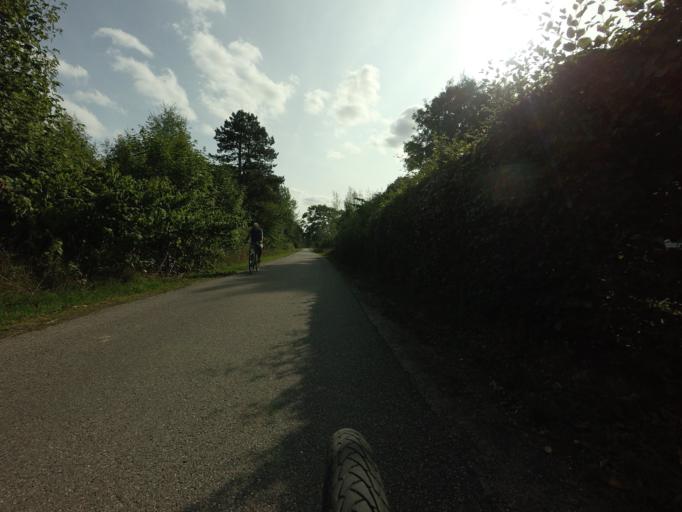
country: DK
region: Zealand
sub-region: Vordingborg Kommune
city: Praesto
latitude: 55.1703
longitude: 12.0976
